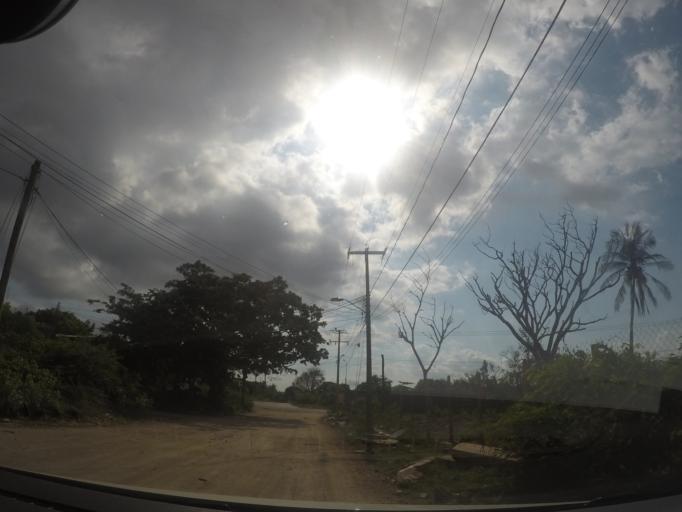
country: MX
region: Oaxaca
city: Juchitan de Zaragoza
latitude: 16.4295
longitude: -95.0324
